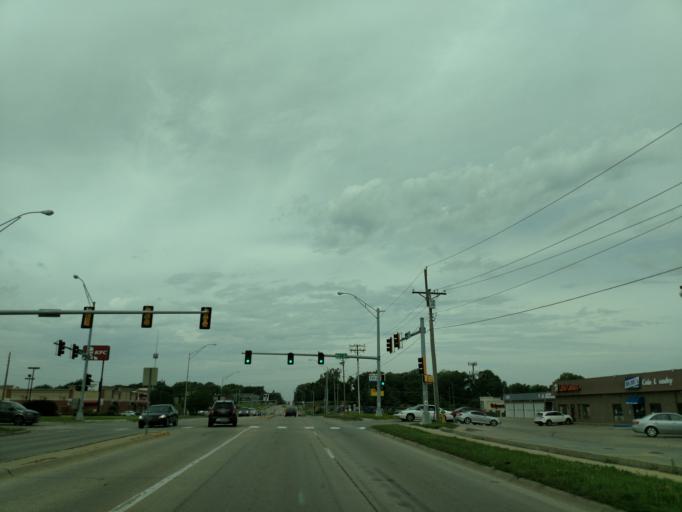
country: US
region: Nebraska
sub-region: Sarpy County
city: La Vista
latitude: 41.1908
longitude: -96.0400
